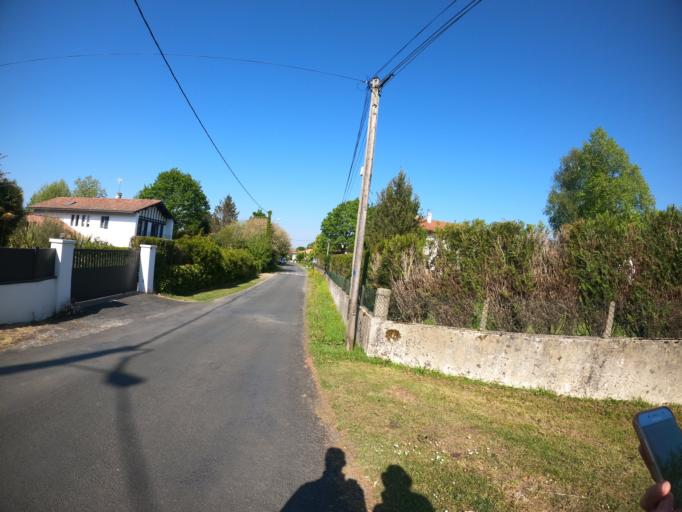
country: FR
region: Aquitaine
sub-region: Departement des Pyrenees-Atlantiques
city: Bassussarry
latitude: 43.4388
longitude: -1.5015
